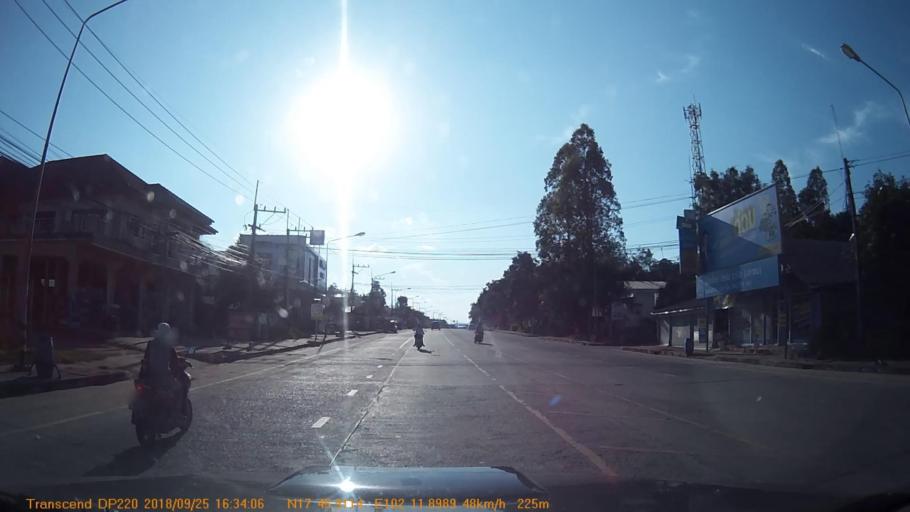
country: TH
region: Changwat Udon Thani
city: Nam Som
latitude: 17.7652
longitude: 102.1983
